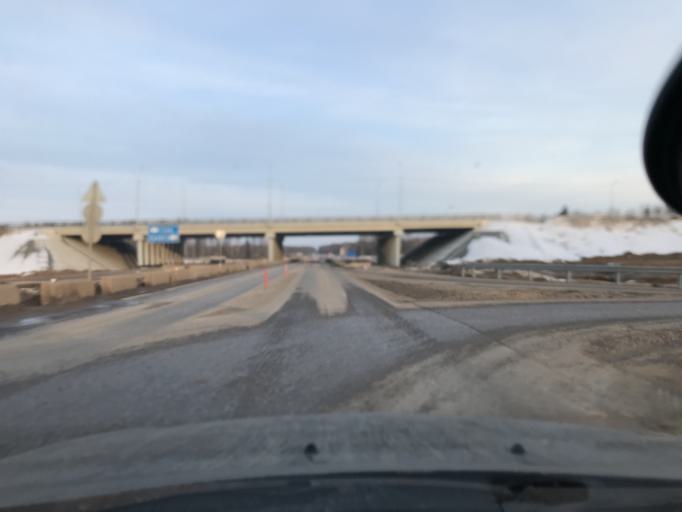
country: RU
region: Kaluga
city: Kaluga
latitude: 54.4600
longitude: 36.2710
